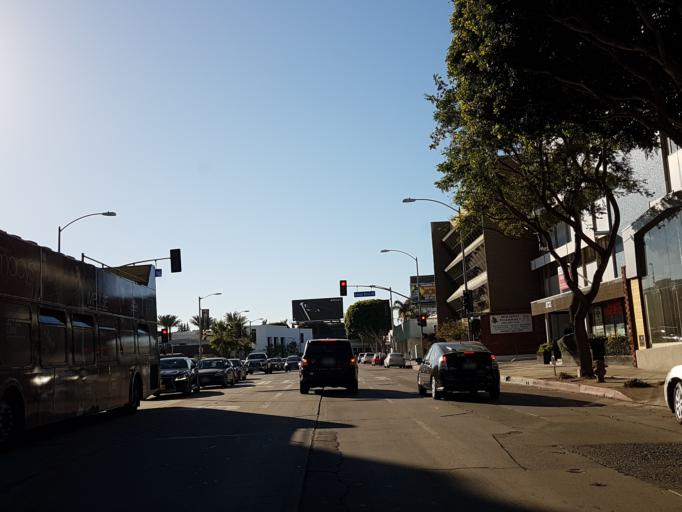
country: US
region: California
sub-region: Los Angeles County
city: Beverly Hills
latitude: 34.0769
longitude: -118.3811
